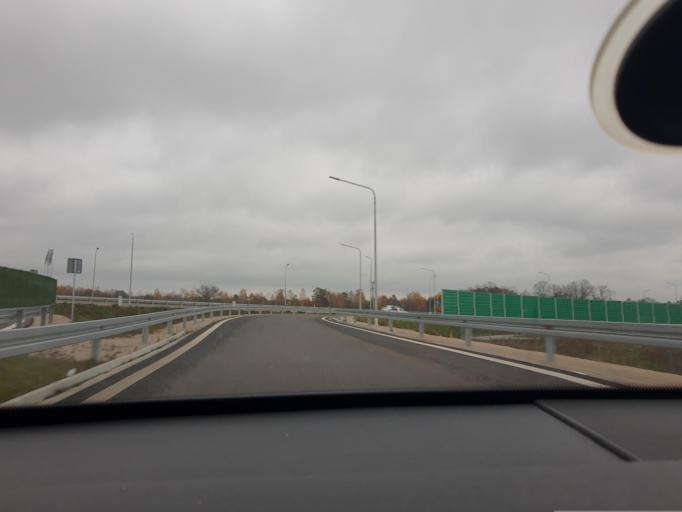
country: PL
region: Lodz Voivodeship
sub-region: Powiat pabianicki
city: Konstantynow Lodzki
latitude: 51.7281
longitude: 19.3548
